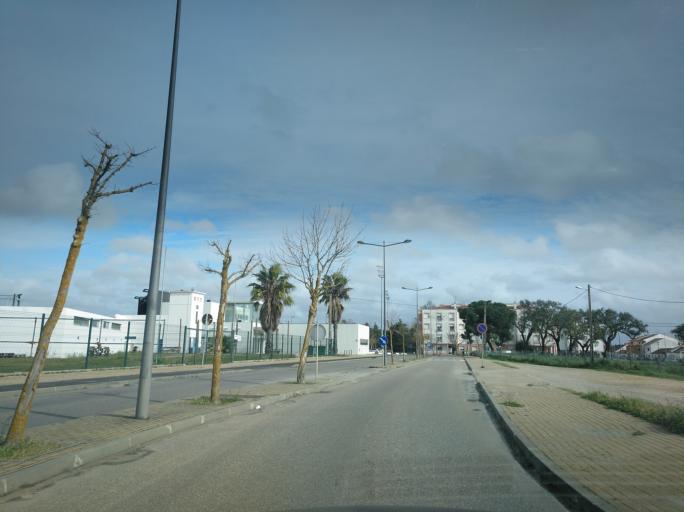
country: PT
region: Setubal
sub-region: Grandola
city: Grandola
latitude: 38.1841
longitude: -8.5663
